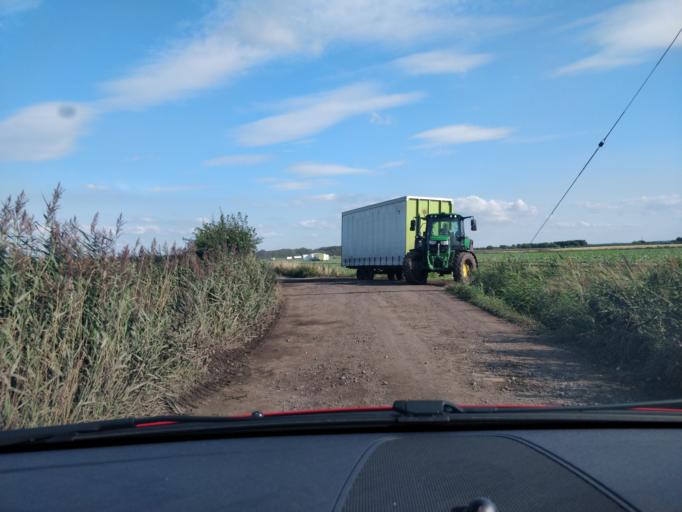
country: GB
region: England
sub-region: Lancashire
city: Banks
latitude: 53.6610
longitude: -2.9154
